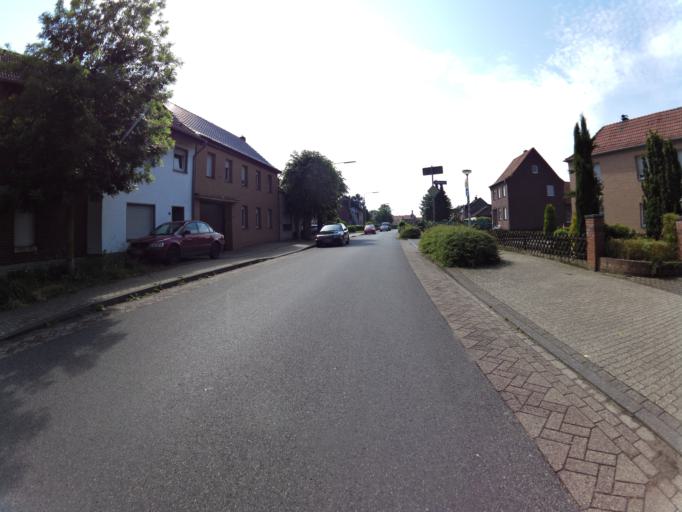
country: DE
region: North Rhine-Westphalia
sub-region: Regierungsbezirk Koln
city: Waldfeucht
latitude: 51.0760
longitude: 5.9949
